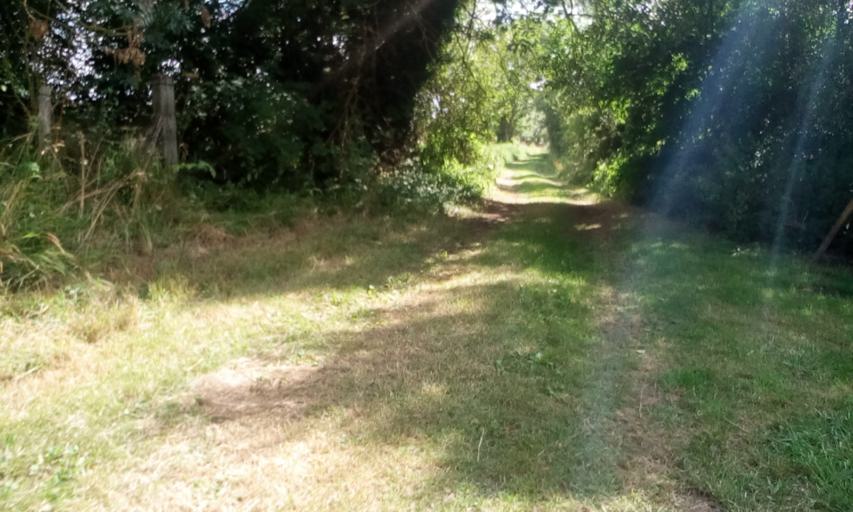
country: FR
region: Lower Normandy
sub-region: Departement du Calvados
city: Moult
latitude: 49.1021
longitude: -0.1882
